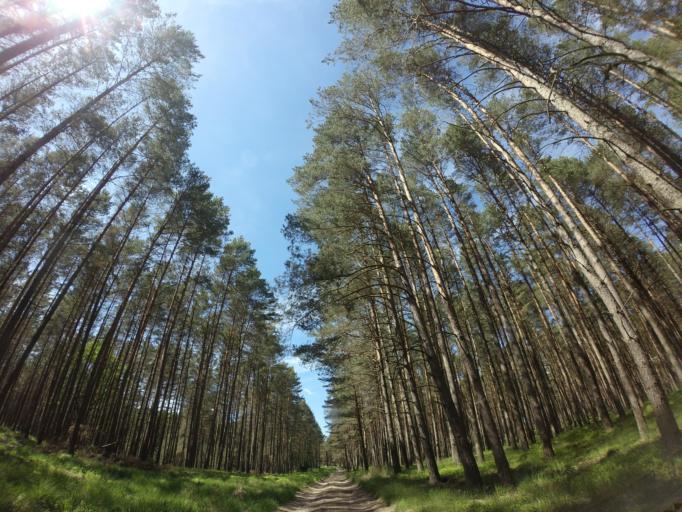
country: PL
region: West Pomeranian Voivodeship
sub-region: Powiat choszczenski
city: Drawno
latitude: 53.1264
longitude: 15.7951
